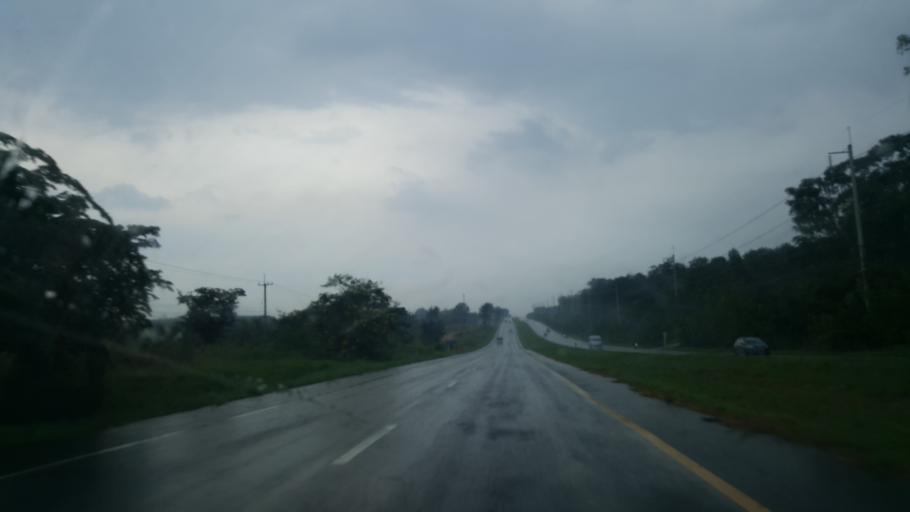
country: TH
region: Chon Buri
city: Ban Talat Bueng
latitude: 12.9712
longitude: 101.0556
